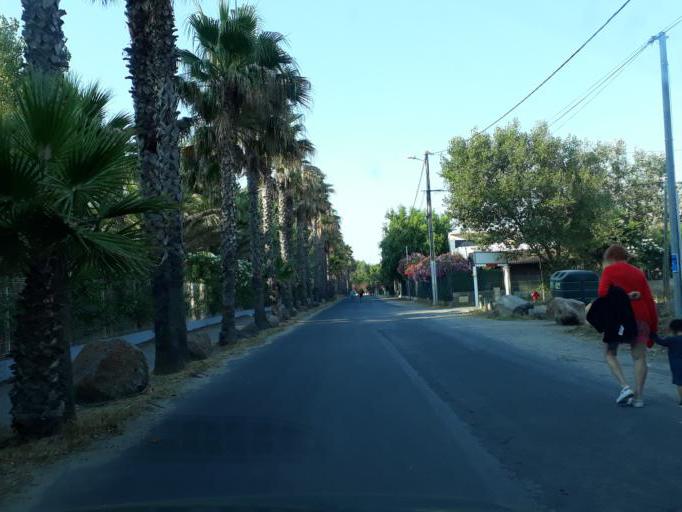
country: FR
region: Languedoc-Roussillon
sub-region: Departement de l'Herault
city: Agde
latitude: 43.2782
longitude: 3.4716
